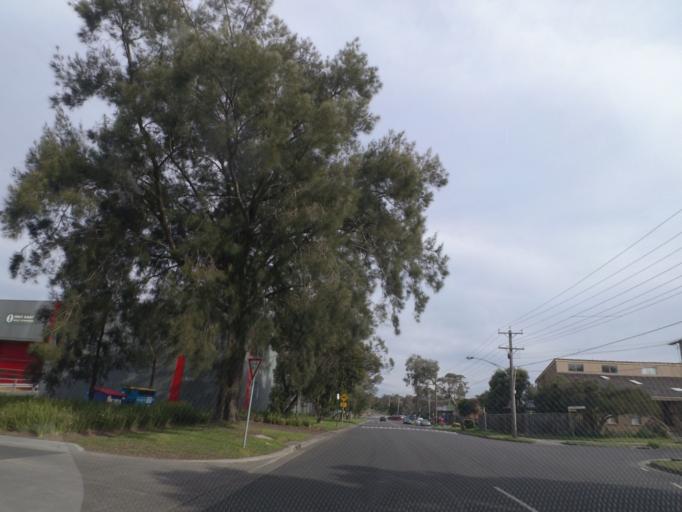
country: AU
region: Victoria
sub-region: Whitehorse
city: Vermont South
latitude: -37.8574
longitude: 145.1982
